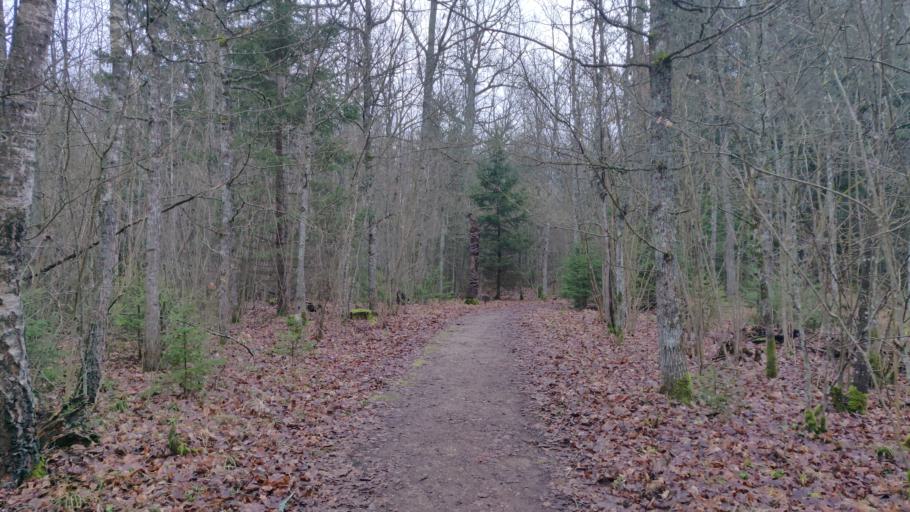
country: LT
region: Vilnius County
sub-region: Vilniaus Rajonas
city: Vievis
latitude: 54.8359
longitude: 24.9538
